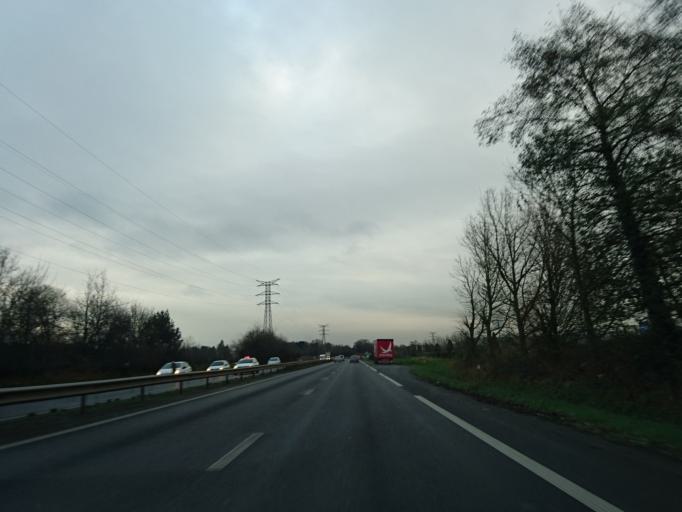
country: FR
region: Brittany
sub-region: Departement d'Ille-et-Vilaine
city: La Chapelle-des-Fougeretz
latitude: 48.1977
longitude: -1.7275
